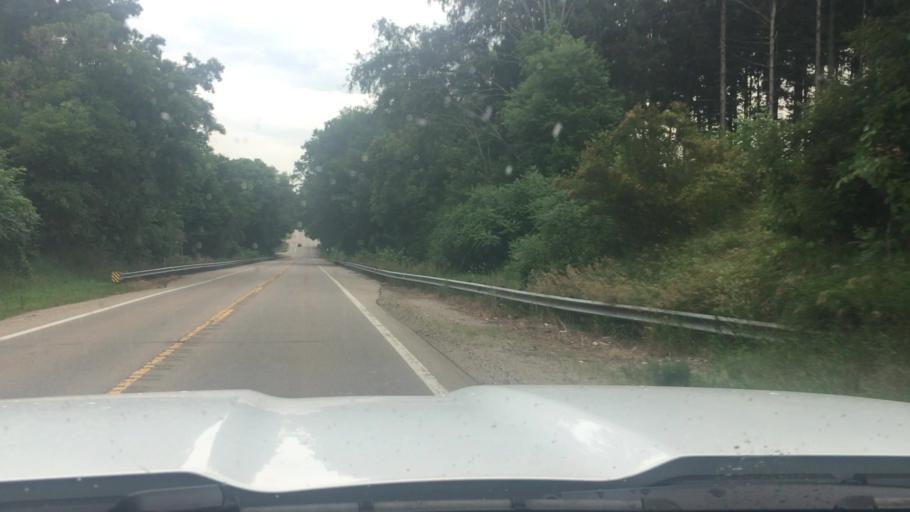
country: US
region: Michigan
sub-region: Ionia County
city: Ionia
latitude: 42.9857
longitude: -85.0921
